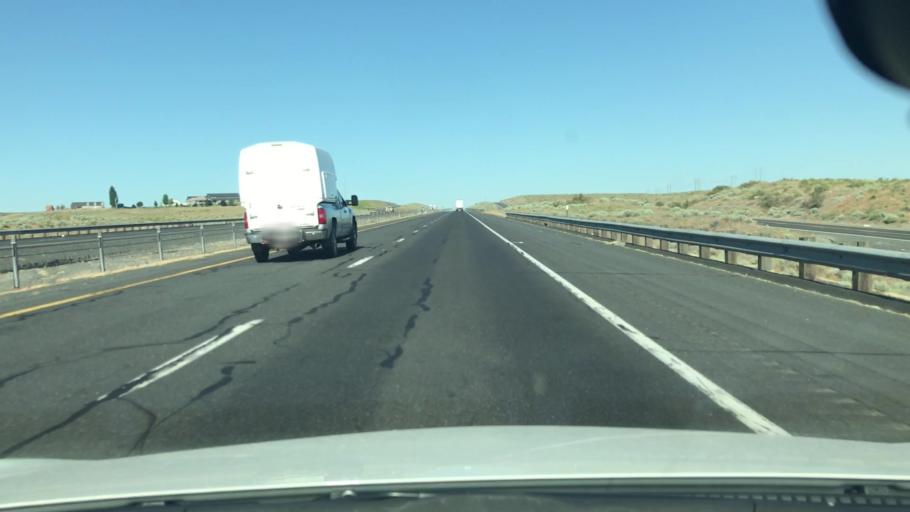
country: US
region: Washington
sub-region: Grant County
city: Cascade Valley
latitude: 47.1042
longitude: -119.4652
